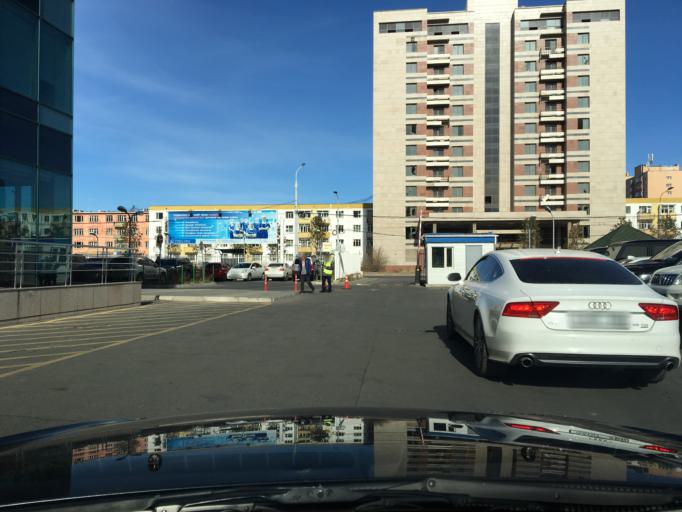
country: MN
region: Ulaanbaatar
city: Ulaanbaatar
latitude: 47.8985
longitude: 106.9058
